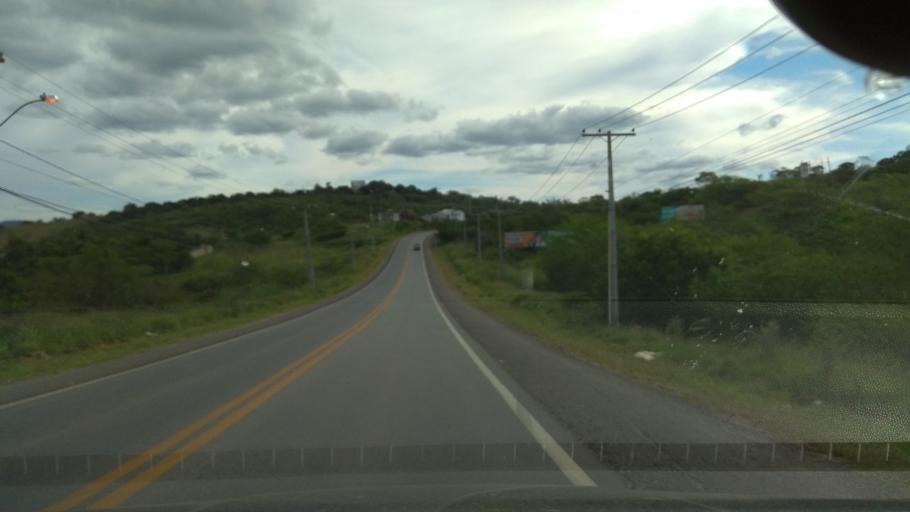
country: BR
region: Bahia
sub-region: Jequie
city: Jequie
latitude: -13.8713
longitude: -40.0467
